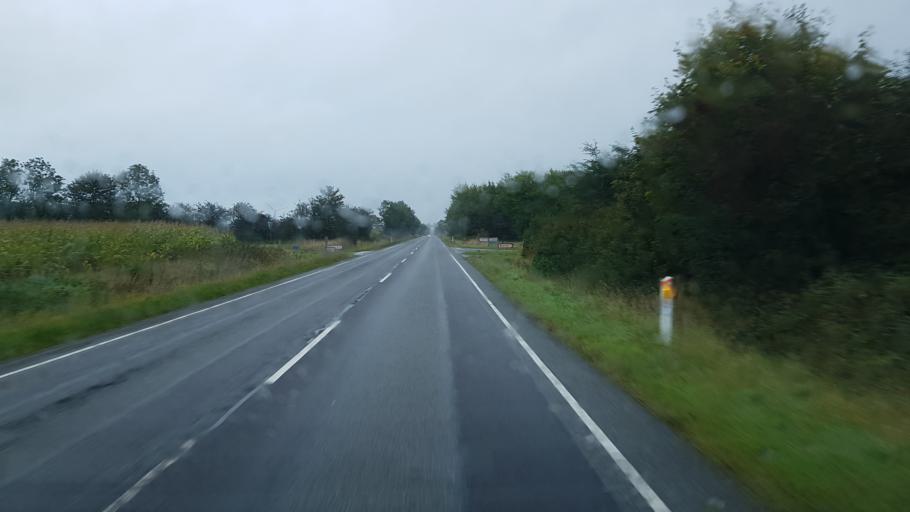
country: DK
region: South Denmark
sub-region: Kolding Kommune
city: Vamdrup
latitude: 55.3483
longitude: 9.2480
